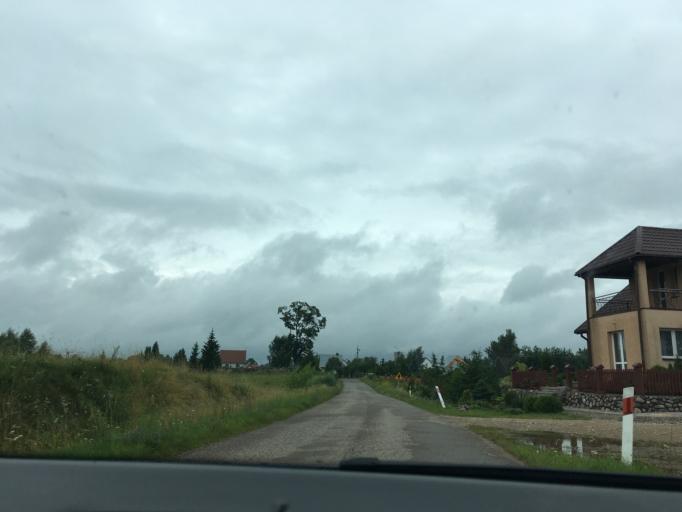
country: PL
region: Podlasie
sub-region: Powiat sejnenski
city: Krasnopol
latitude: 54.1095
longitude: 23.2134
